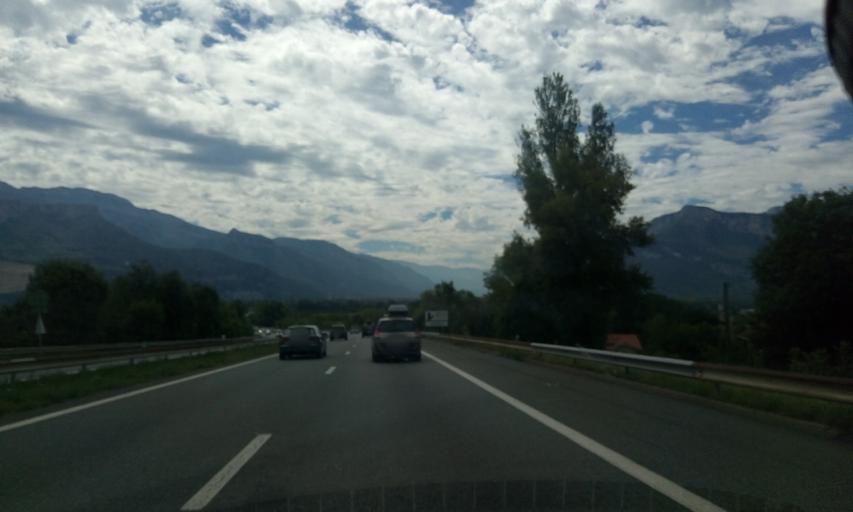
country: FR
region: Rhone-Alpes
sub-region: Departement de l'Isere
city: Saint-Jean-de-Moirans
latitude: 45.3387
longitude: 5.5768
